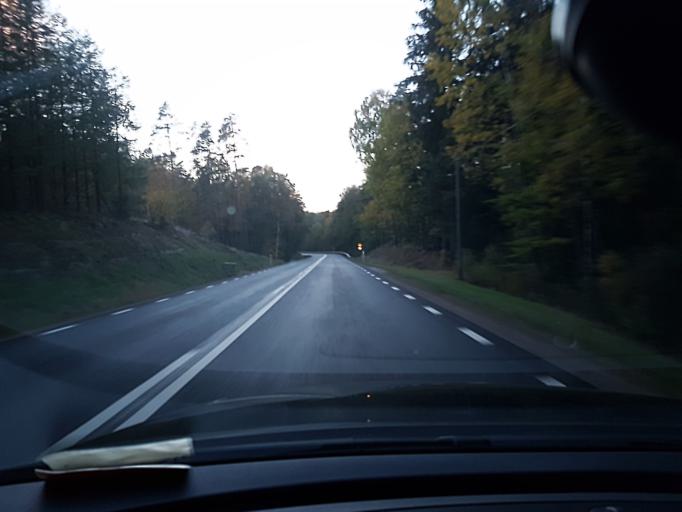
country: SE
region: Halland
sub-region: Laholms Kommun
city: Veinge
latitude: 56.7222
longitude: 13.1636
